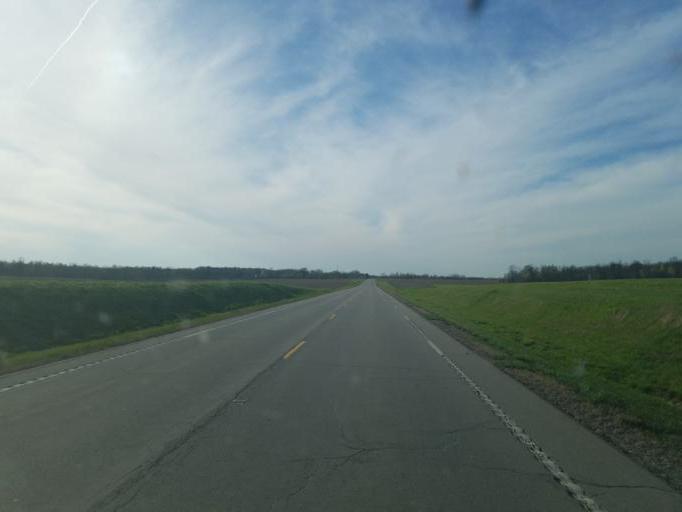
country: US
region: Ohio
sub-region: Huron County
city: New London
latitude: 41.0759
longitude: -82.4627
